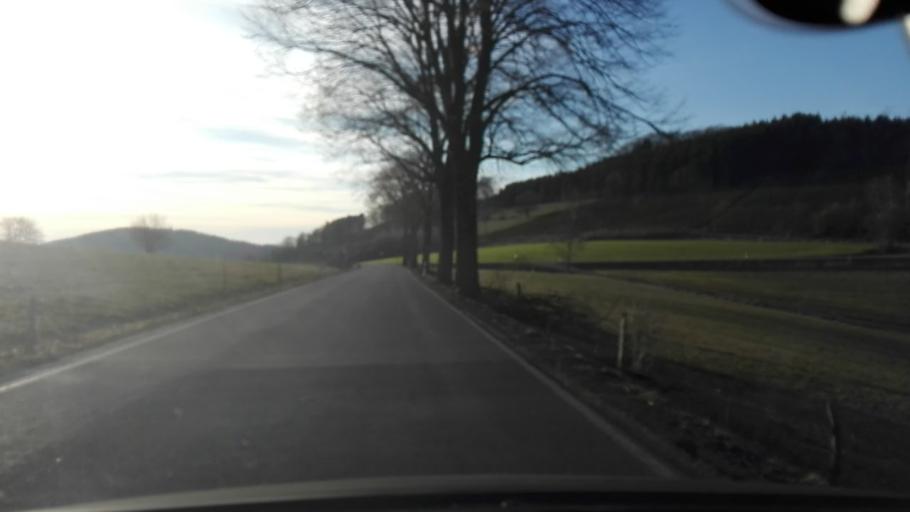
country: DE
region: North Rhine-Westphalia
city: Eslohe
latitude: 51.1719
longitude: 8.1617
